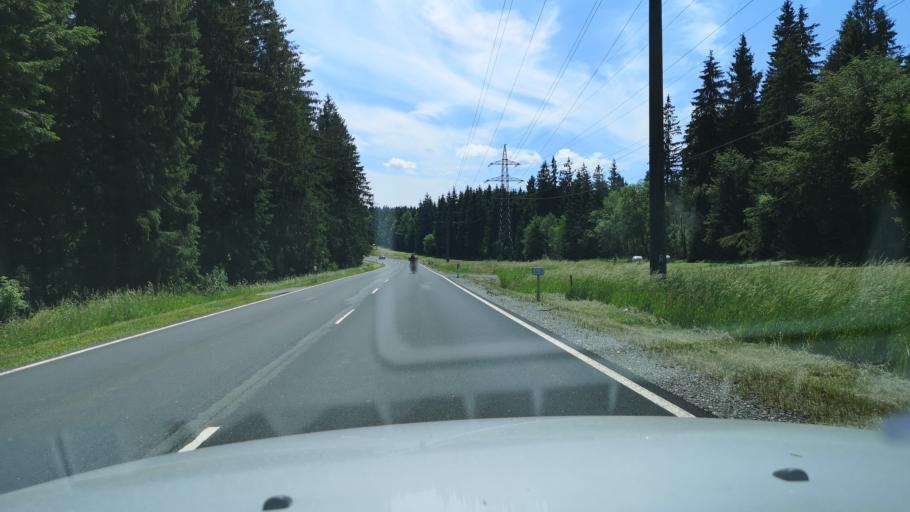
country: DE
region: Bavaria
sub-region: Upper Franconia
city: Tettau
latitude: 50.4759
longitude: 11.3066
